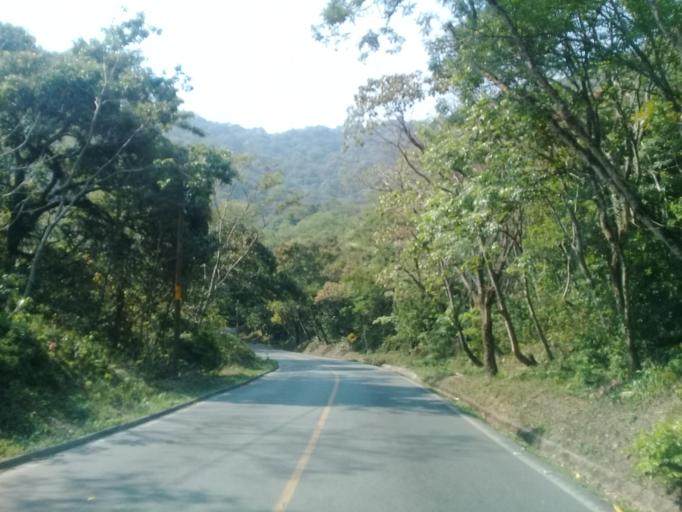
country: MX
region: Veracruz
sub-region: Ixtaczoquitlan
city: Campo Chico
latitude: 18.8441
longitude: -97.0297
